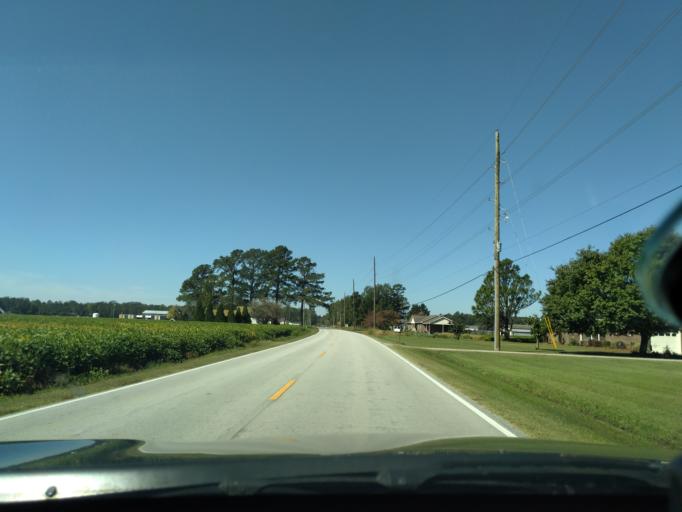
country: US
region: North Carolina
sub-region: Beaufort County
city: River Road
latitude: 35.5757
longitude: -76.9369
